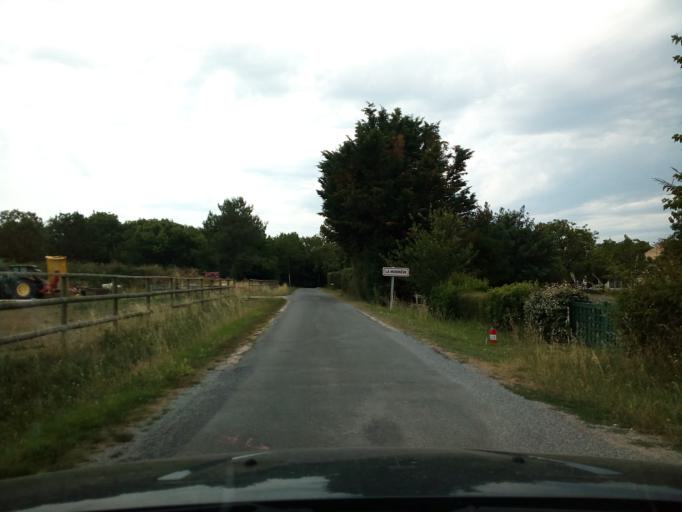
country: FR
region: Poitou-Charentes
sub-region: Departement de la Charente-Maritime
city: Dolus-d'Oleron
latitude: 45.9293
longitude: -1.2667
